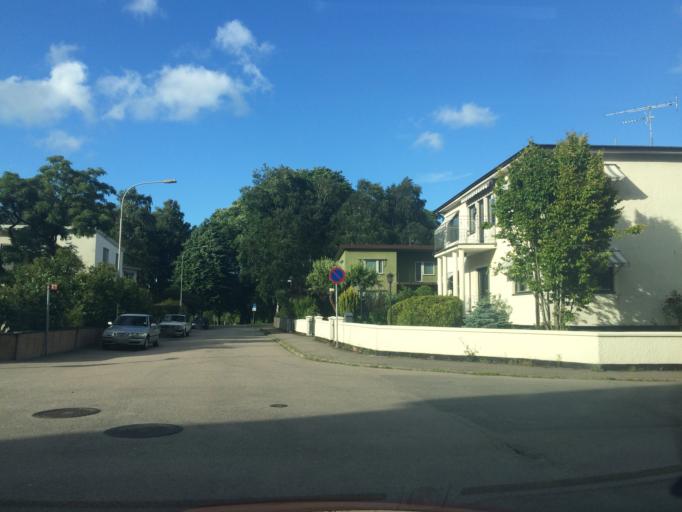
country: SE
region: Vaestra Goetaland
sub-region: Vanersborgs Kommun
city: Vanersborg
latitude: 58.3817
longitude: 12.3321
